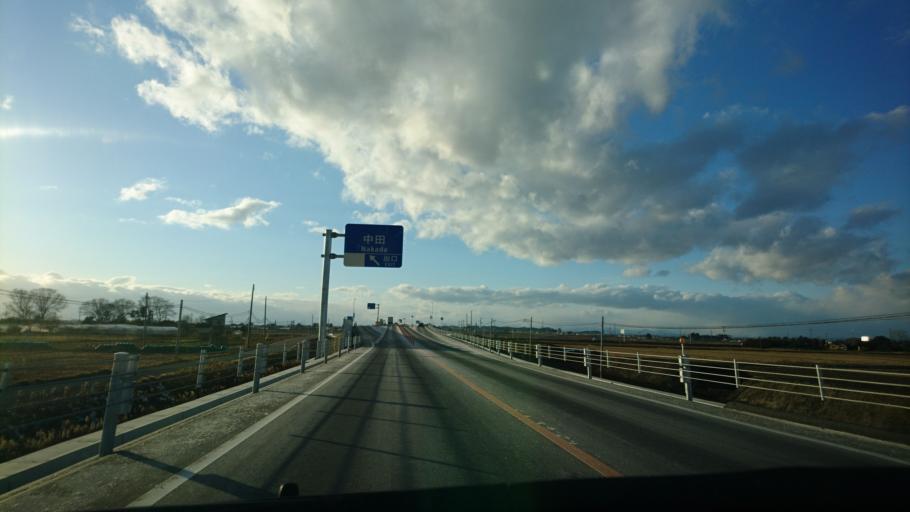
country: JP
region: Miyagi
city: Wakuya
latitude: 38.6860
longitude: 141.2369
